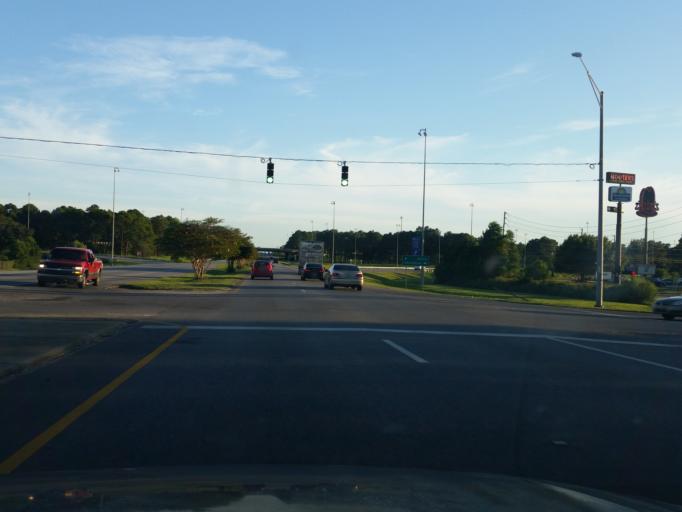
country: US
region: Alabama
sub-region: Mobile County
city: Tillmans Corner
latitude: 30.5857
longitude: -88.1700
